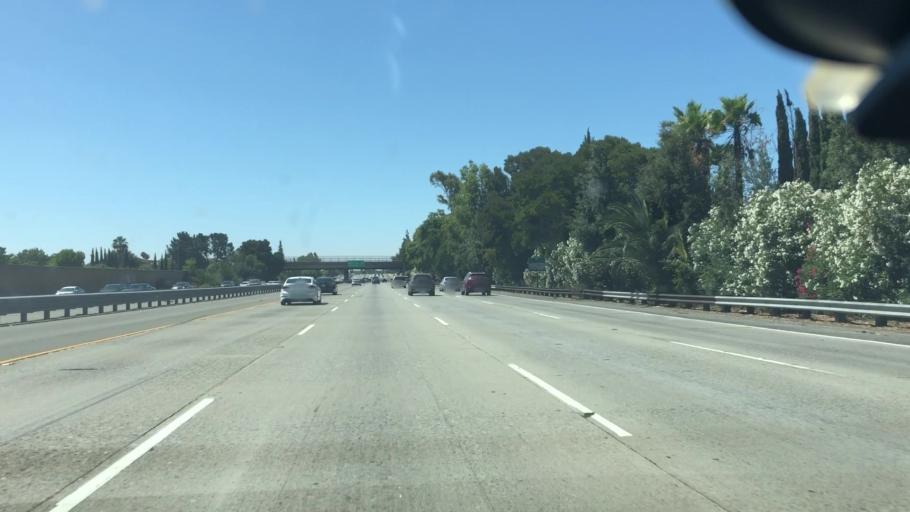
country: US
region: California
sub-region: Santa Clara County
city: Milpitas
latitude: 37.4084
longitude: -121.8786
